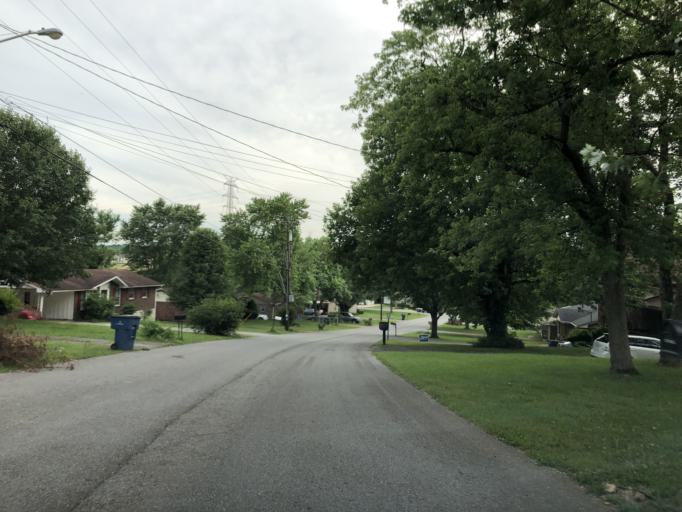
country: US
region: Tennessee
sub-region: Davidson County
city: Goodlettsville
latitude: 36.2921
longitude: -86.7166
